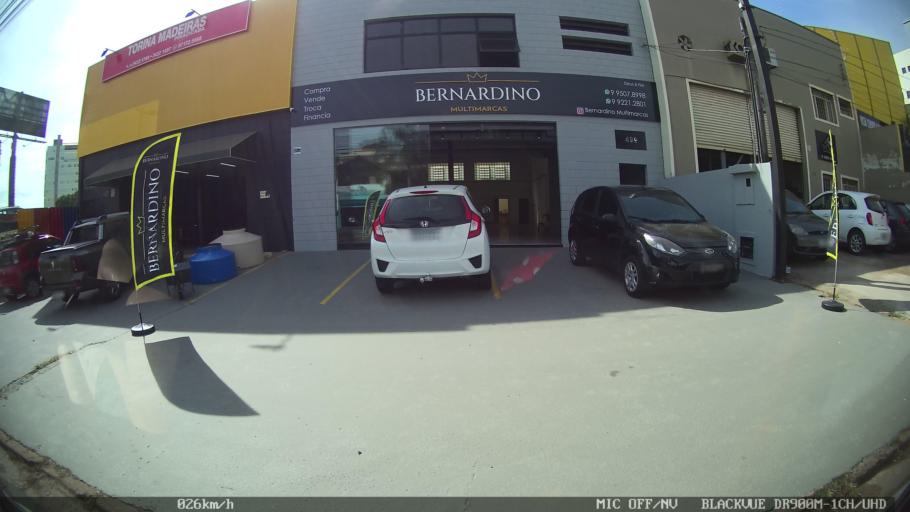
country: BR
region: Sao Paulo
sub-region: Piracicaba
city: Piracicaba
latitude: -22.7312
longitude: -47.6640
